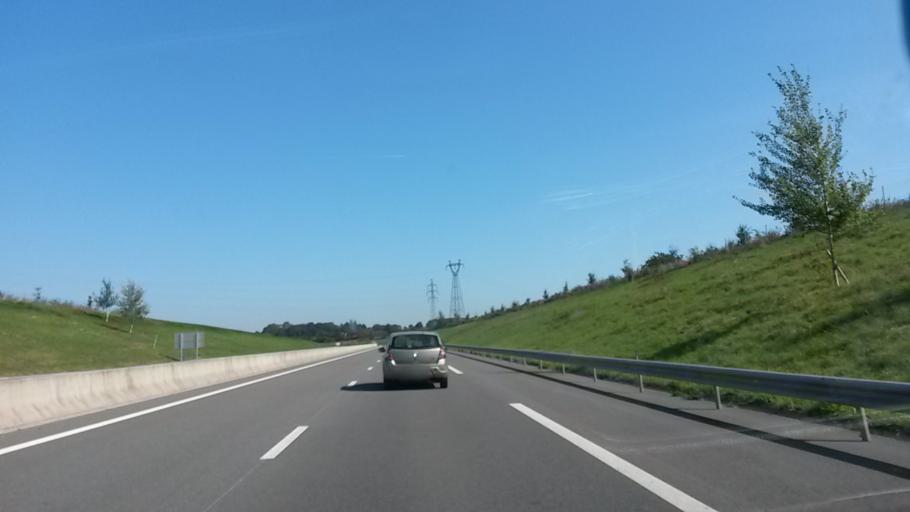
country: FR
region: Nord-Pas-de-Calais
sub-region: Departement du Nord
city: Louvroil
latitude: 50.2266
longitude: 3.9596
